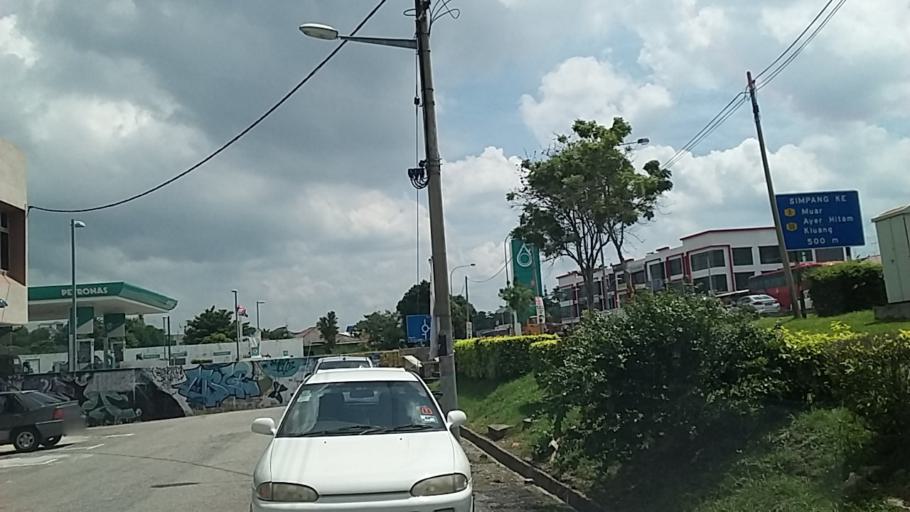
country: MY
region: Johor
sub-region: Daerah Batu Pahat
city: Batu Pahat
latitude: 1.8436
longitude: 102.9423
